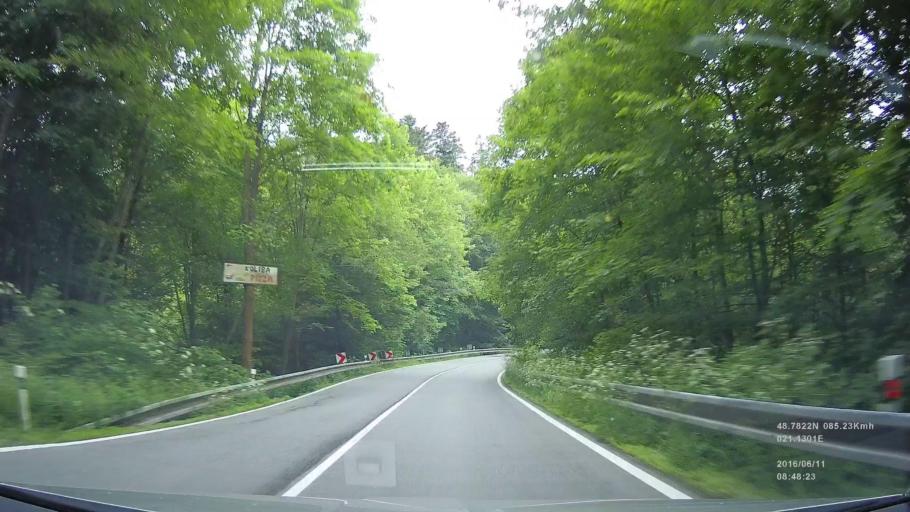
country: SK
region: Kosicky
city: Kosice
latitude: 48.7775
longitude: 21.1368
